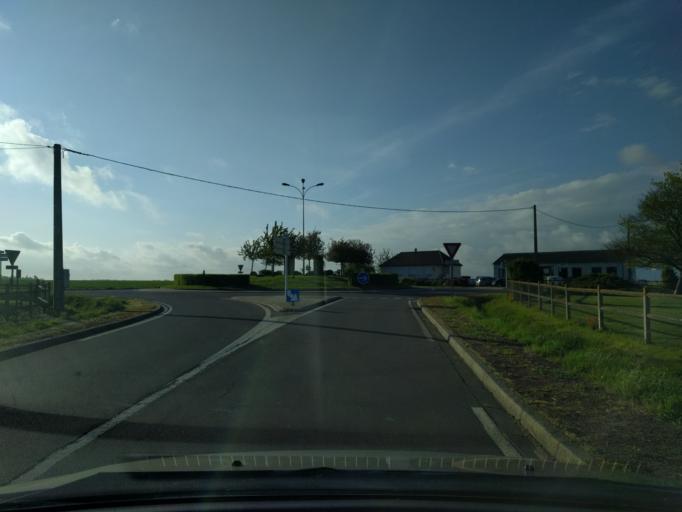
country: FR
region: Haute-Normandie
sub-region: Departement de l'Eure
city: Damville
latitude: 48.9071
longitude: 1.0233
